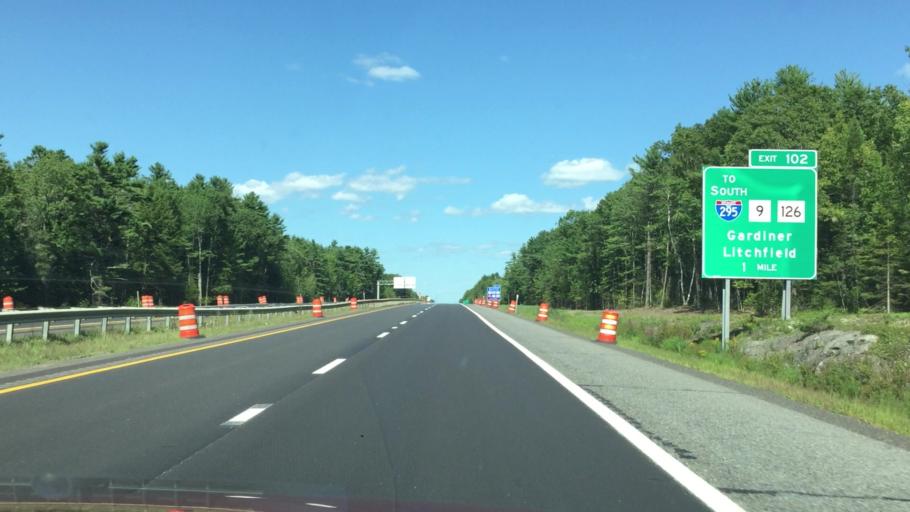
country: US
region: Maine
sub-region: Kennebec County
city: Gardiner
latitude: 44.1961
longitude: -69.8443
